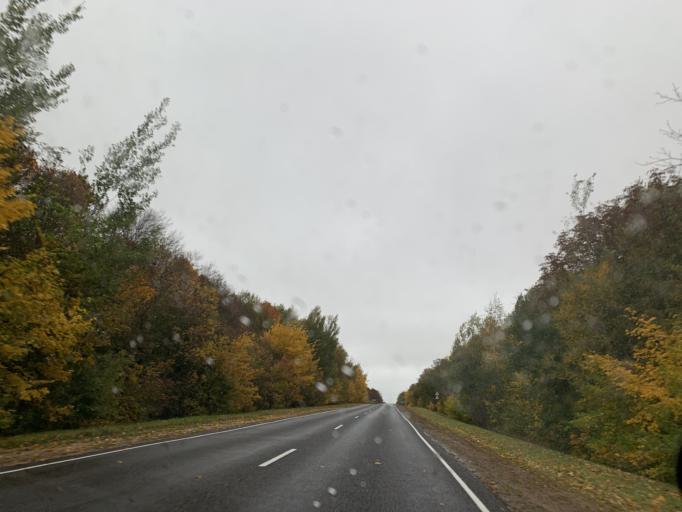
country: BY
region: Minsk
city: Haradzyeya
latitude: 53.3881
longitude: 26.5705
